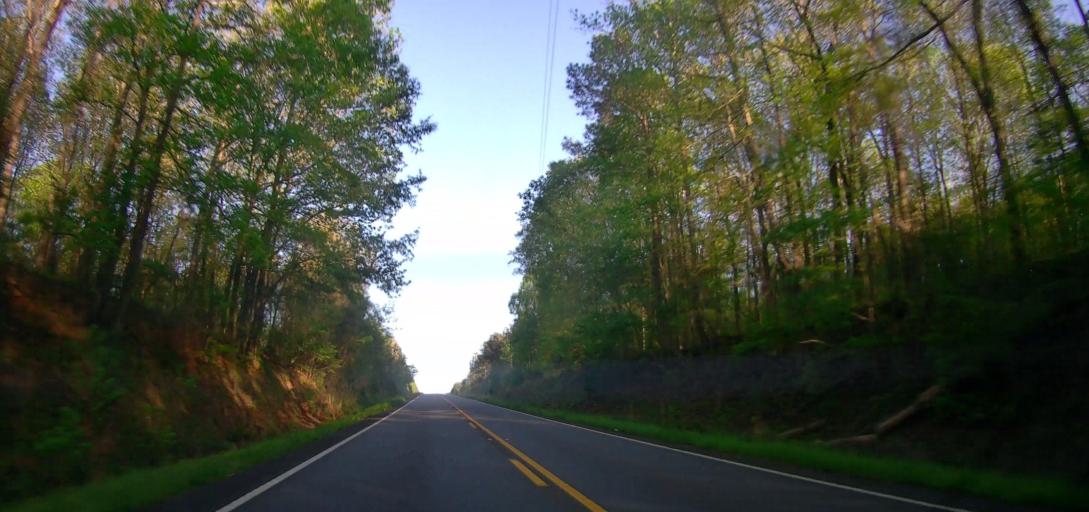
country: US
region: Georgia
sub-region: Schley County
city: Ellaville
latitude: 32.3534
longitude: -84.3827
